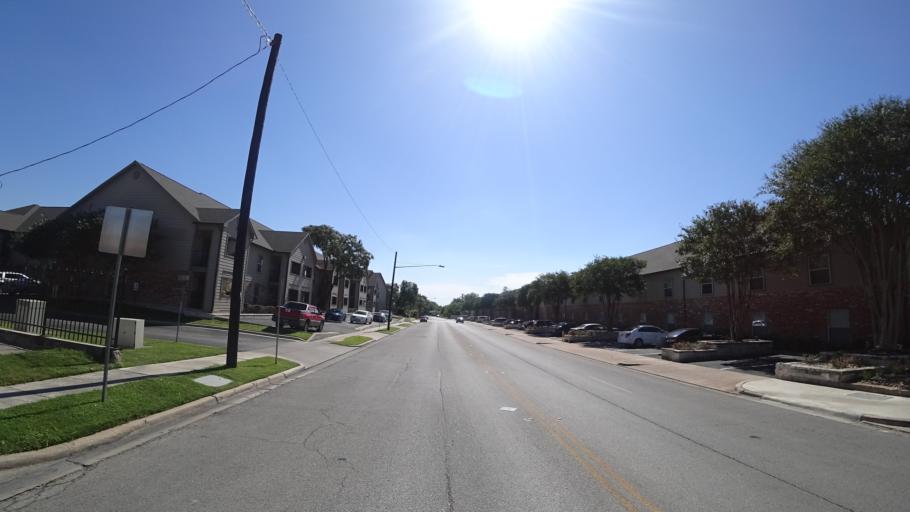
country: US
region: Texas
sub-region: Travis County
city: Austin
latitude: 30.3112
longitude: -97.7067
